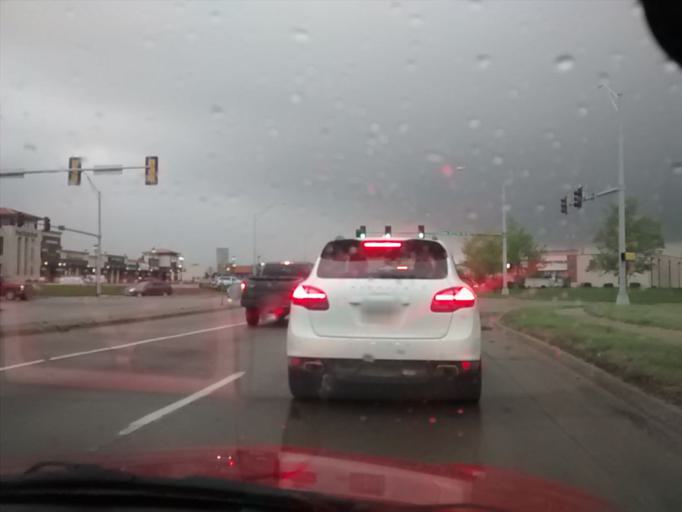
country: US
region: Nebraska
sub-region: Douglas County
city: Ralston
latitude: 41.2016
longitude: -96.0237
